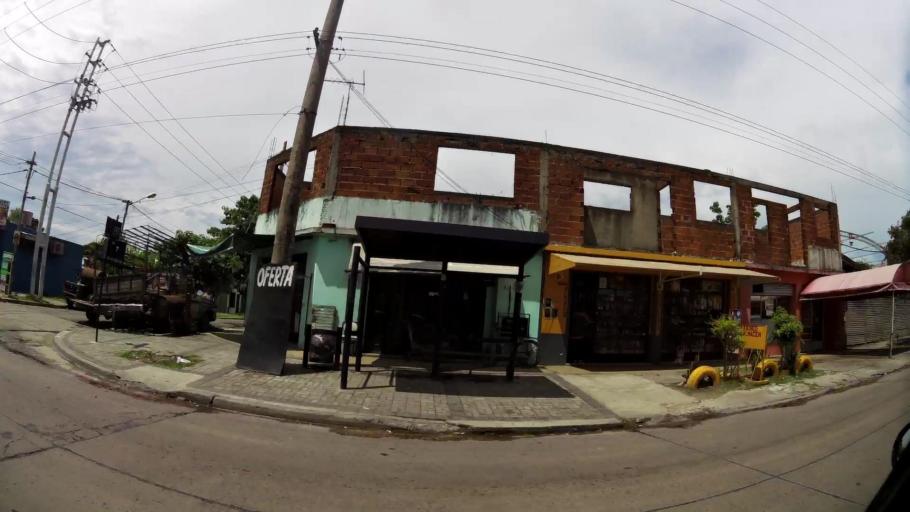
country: AR
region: Buenos Aires
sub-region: Partido de Quilmes
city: Quilmes
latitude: -34.7672
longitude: -58.2373
